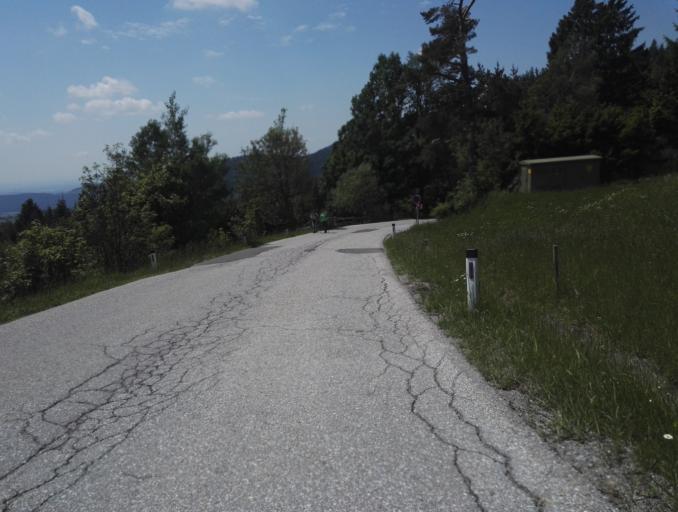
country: AT
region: Styria
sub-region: Politischer Bezirk Graz-Umgebung
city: Sankt Radegund bei Graz
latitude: 47.1926
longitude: 15.4845
